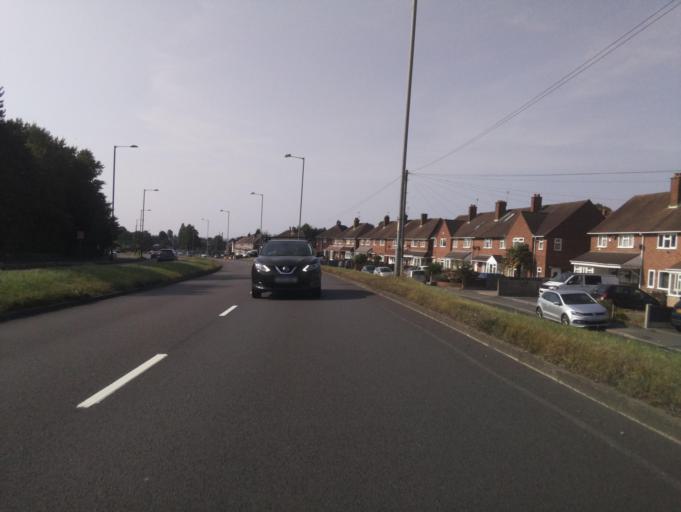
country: GB
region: England
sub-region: Walsall
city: Streetly
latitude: 52.5589
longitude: -1.8967
